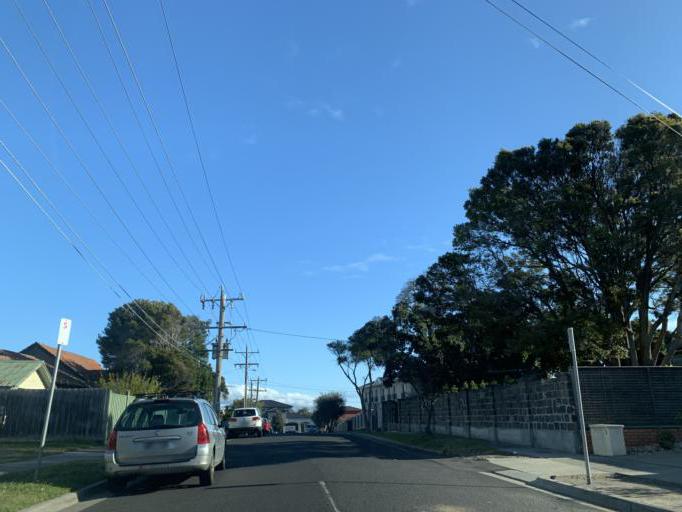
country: AU
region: Victoria
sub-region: Kingston
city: Mentone
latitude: -37.9875
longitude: 145.0658
